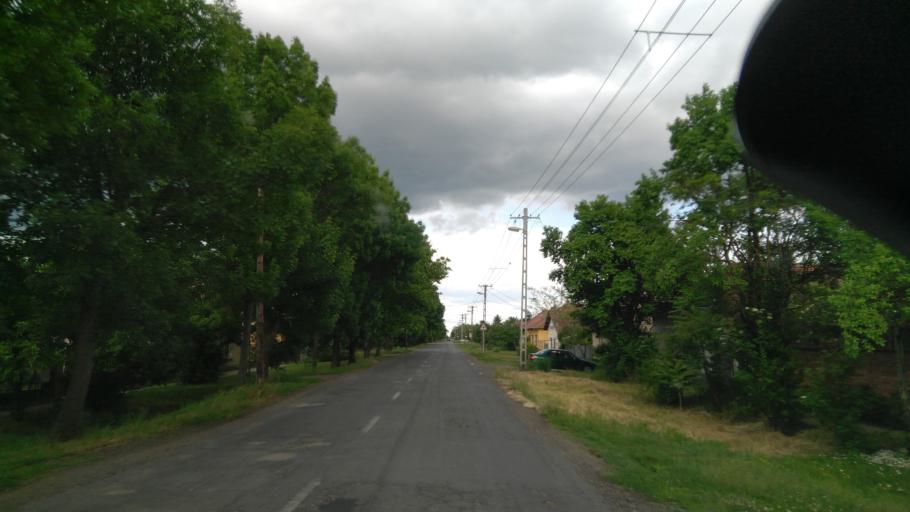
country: HU
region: Bekes
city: Gadoros
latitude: 46.6712
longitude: 20.6031
